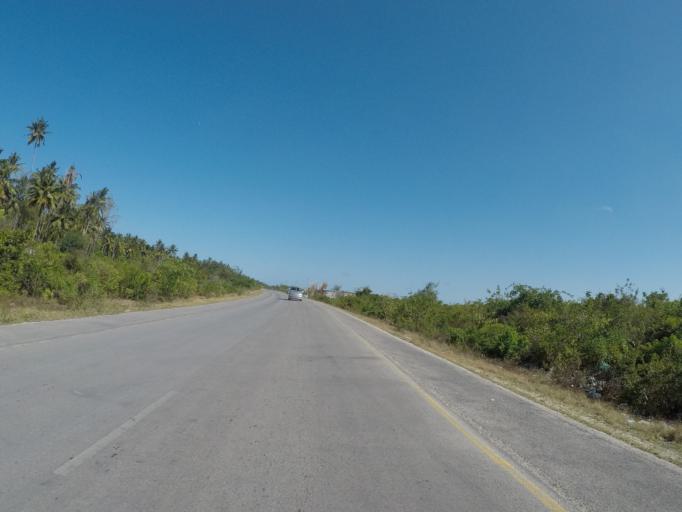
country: TZ
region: Zanzibar Central/South
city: Nganane
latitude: -6.2729
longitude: 39.5328
